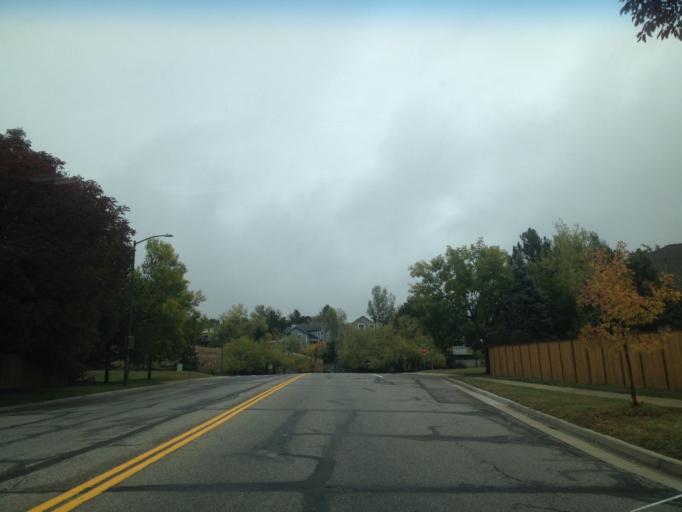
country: US
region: Colorado
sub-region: Boulder County
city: Louisville
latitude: 39.9759
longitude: -105.1535
